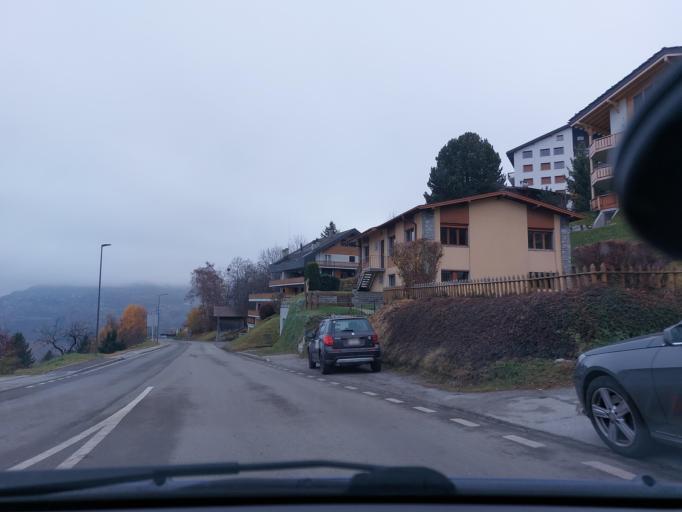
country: CH
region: Valais
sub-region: Conthey District
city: Basse-Nendaz
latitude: 46.1840
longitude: 7.2962
